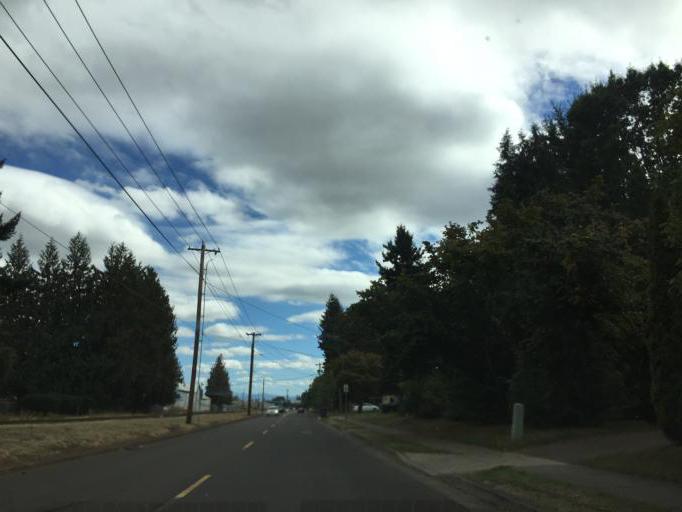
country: US
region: Oregon
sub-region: Marion County
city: Woodburn
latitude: 45.1377
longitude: -122.8499
